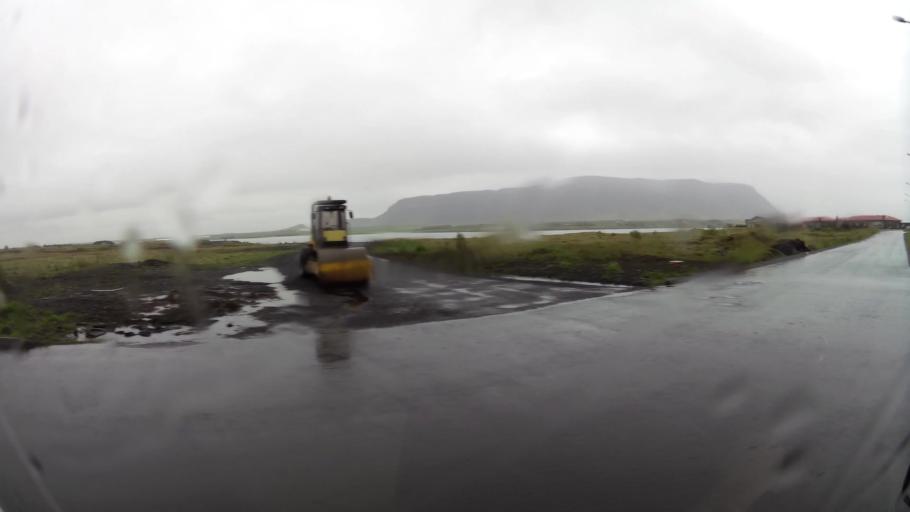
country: IS
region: South
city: Selfoss
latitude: 63.9309
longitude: -21.0268
